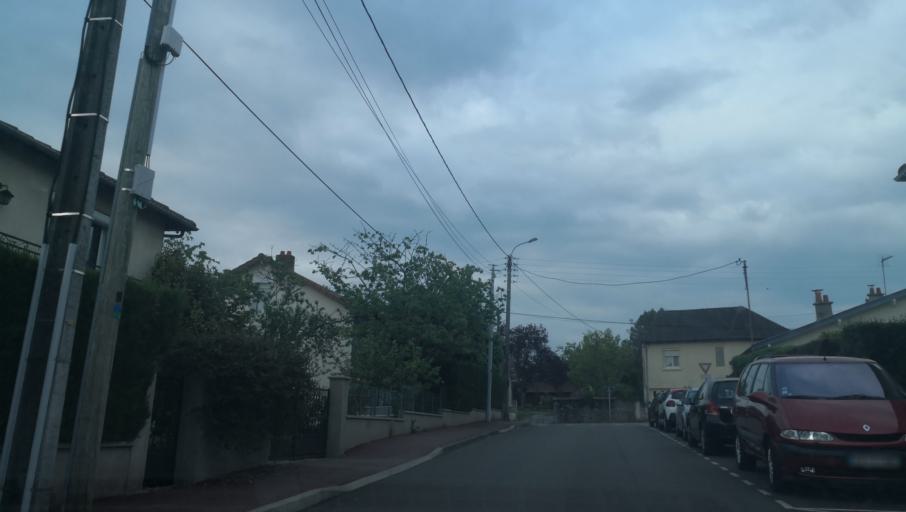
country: FR
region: Limousin
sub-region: Departement de la Haute-Vienne
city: Limoges
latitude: 45.8287
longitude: 1.2332
